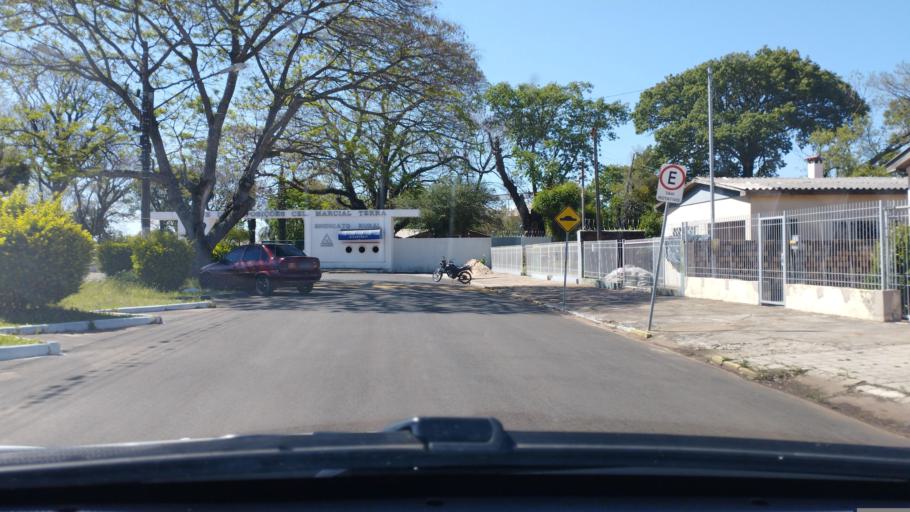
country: BR
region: Rio Grande do Sul
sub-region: Tupancireta
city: Tupancireta
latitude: -29.0751
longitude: -53.8393
